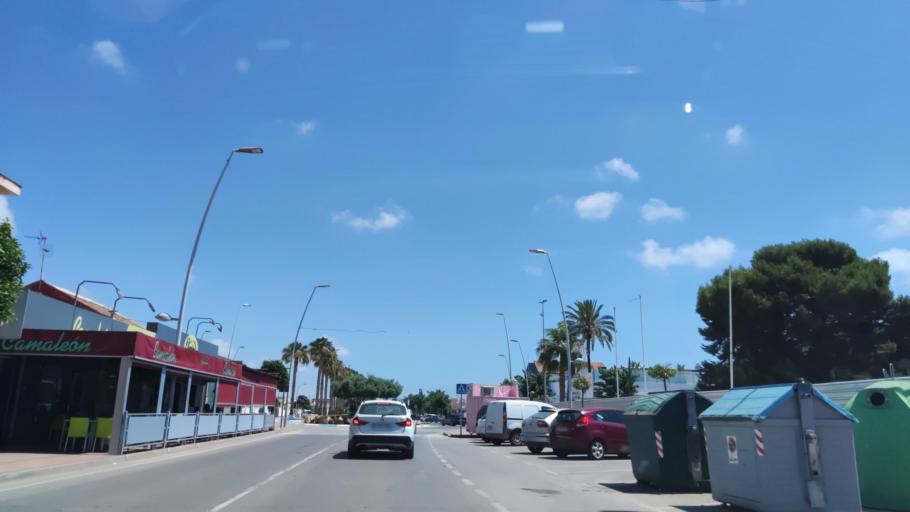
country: ES
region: Murcia
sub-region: Murcia
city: Los Alcazares
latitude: 37.7585
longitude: -0.8388
